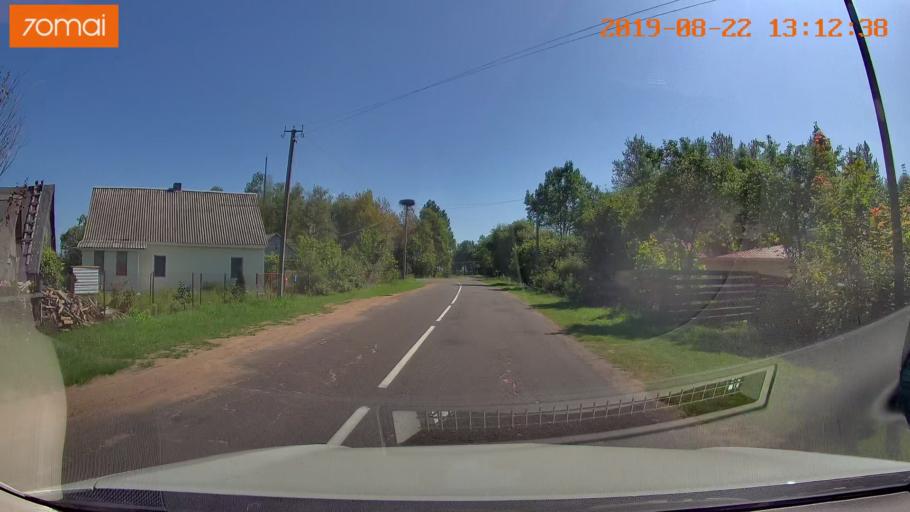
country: BY
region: Minsk
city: Prawdzinski
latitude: 53.2681
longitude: 27.8662
